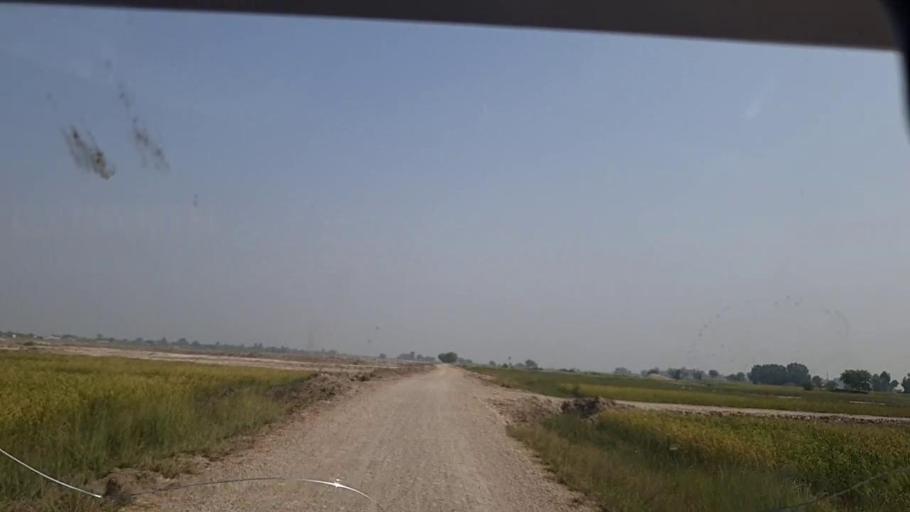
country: PK
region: Sindh
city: Shikarpur
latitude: 28.0513
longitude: 68.6617
